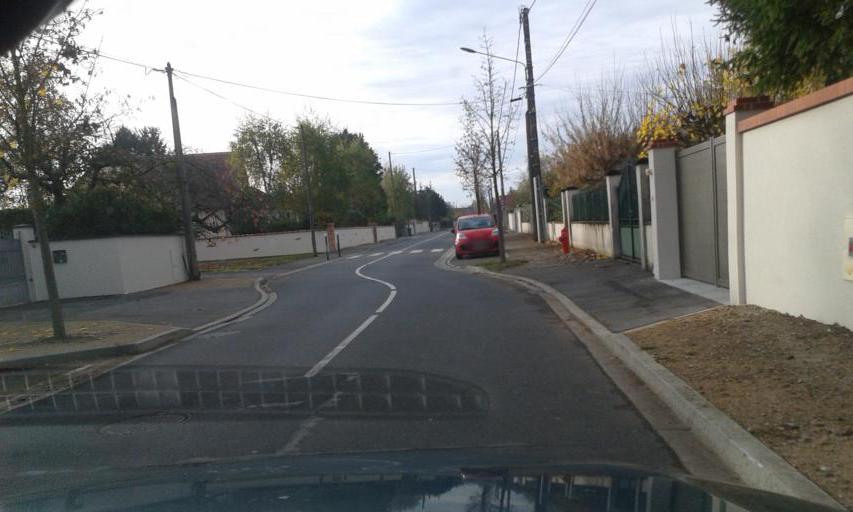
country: FR
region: Centre
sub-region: Departement du Loiret
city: Olivet
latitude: 47.8547
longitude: 1.8941
